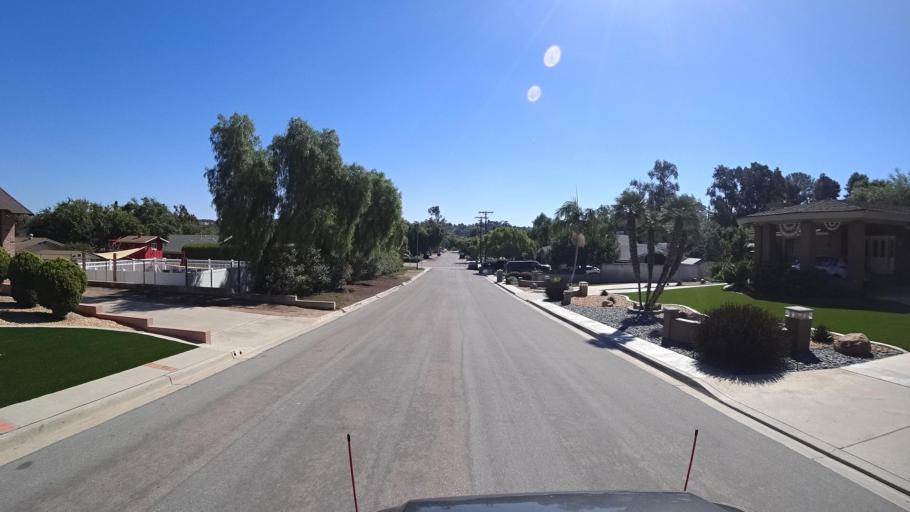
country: US
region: California
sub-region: San Diego County
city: Bonita
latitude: 32.6592
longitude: -117.0510
